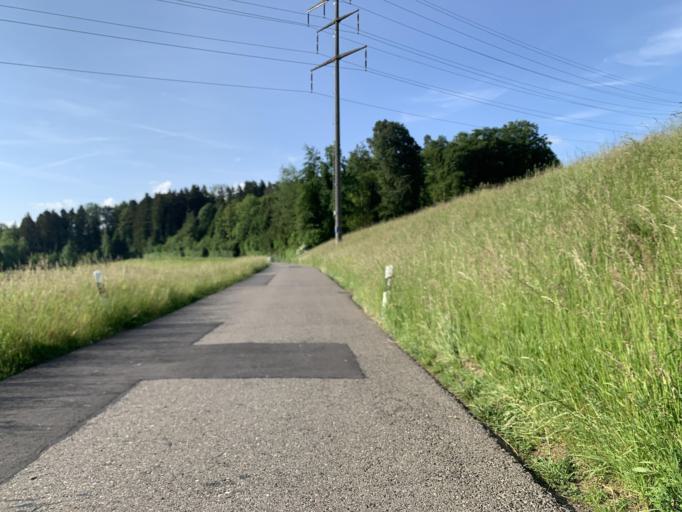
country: CH
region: Zurich
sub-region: Bezirk Hinwil
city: Gossau
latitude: 47.3188
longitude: 8.7415
